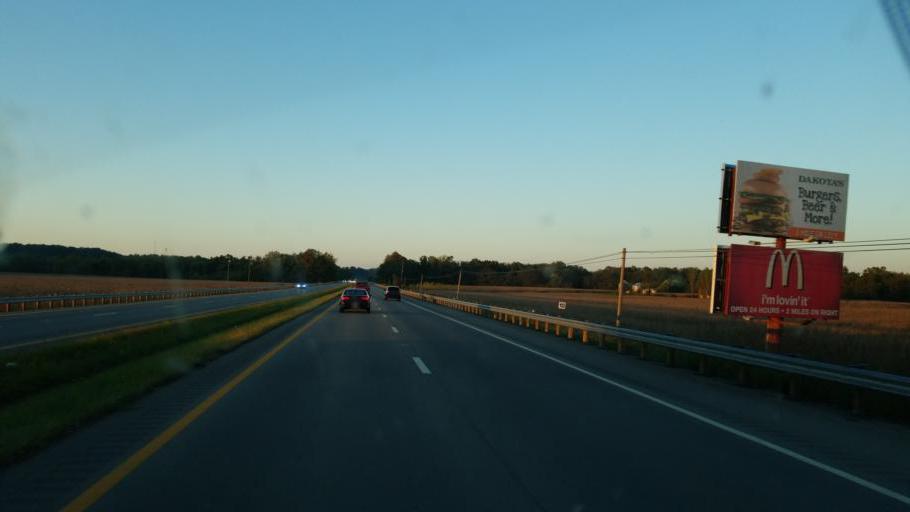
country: US
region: Ohio
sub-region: Pike County
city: Piketon
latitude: 39.0940
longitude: -83.0008
